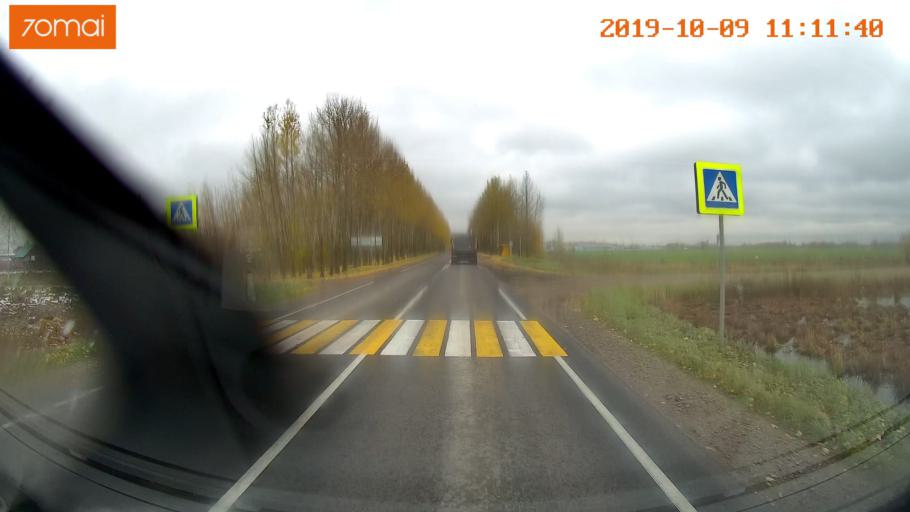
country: RU
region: Vologda
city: Vologda
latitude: 59.1703
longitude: 39.8228
